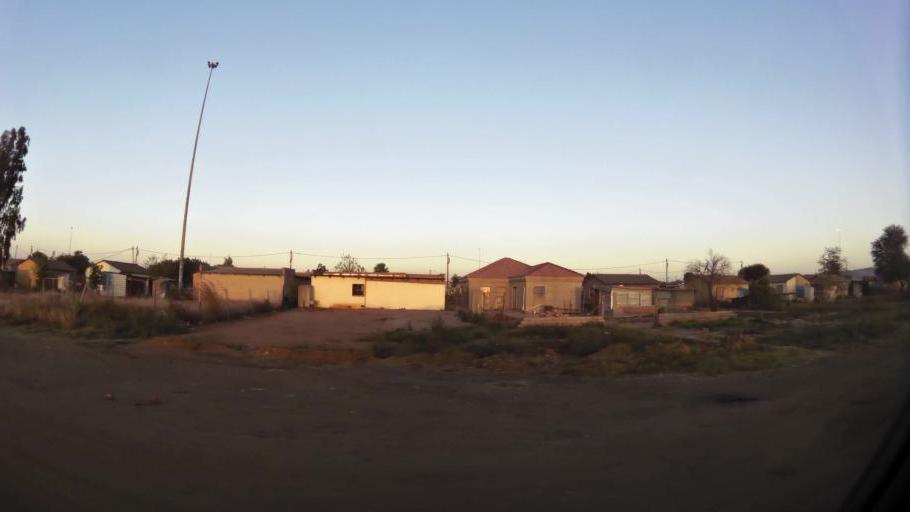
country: ZA
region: North-West
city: Ga-Rankuwa
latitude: -25.5865
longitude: 28.0455
